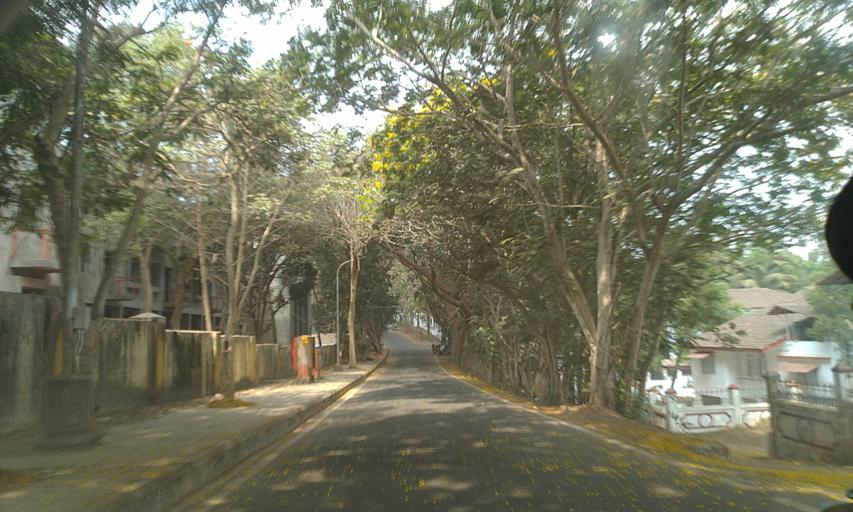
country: IN
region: Goa
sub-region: North Goa
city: Panaji
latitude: 15.4888
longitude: 73.8287
